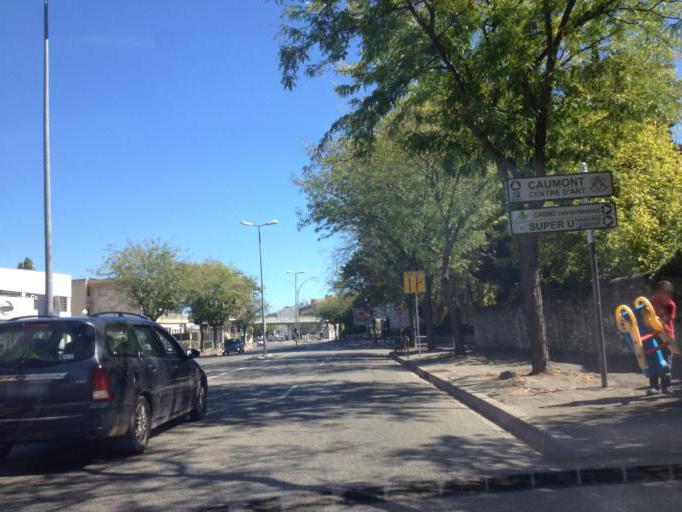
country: FR
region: Provence-Alpes-Cote d'Azur
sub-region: Departement des Bouches-du-Rhone
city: Aix-en-Provence
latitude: 43.5282
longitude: 5.4306
